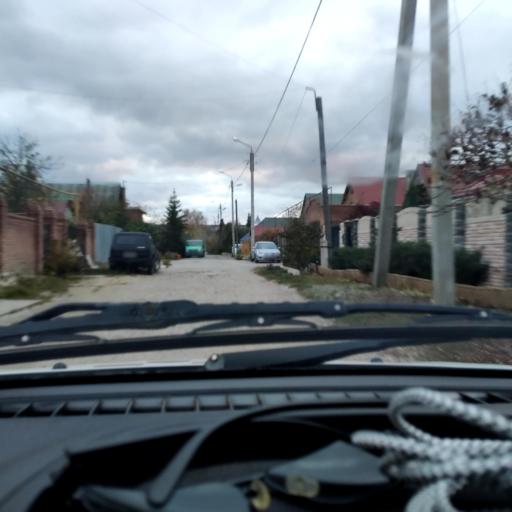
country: RU
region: Samara
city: Tol'yatti
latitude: 53.5219
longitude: 49.4067
